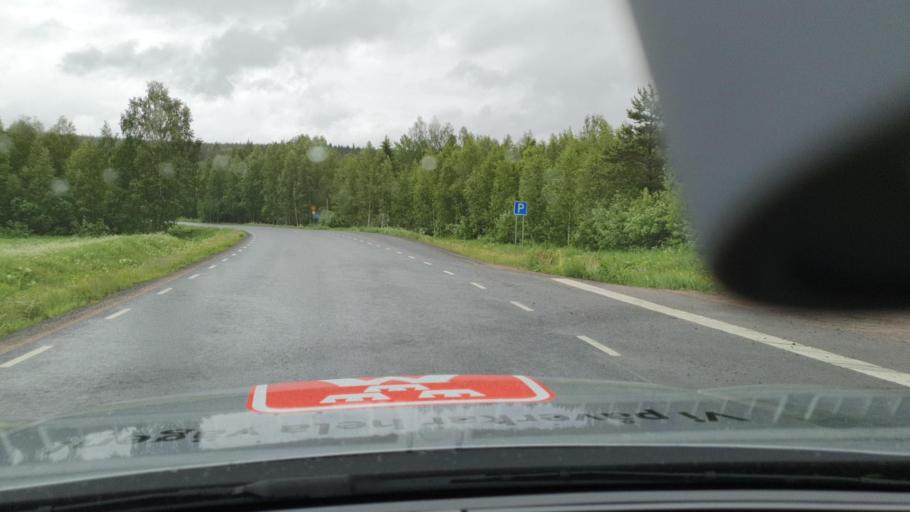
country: FI
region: Lapland
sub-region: Torniolaakso
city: Ylitornio
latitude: 66.1861
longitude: 23.7202
